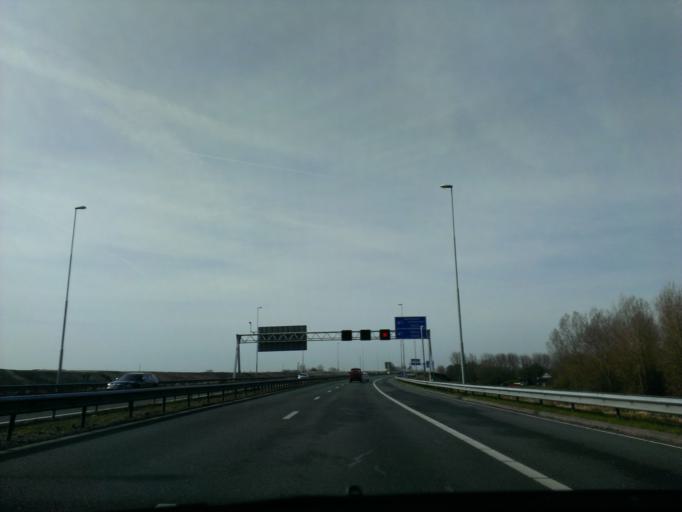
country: NL
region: North Holland
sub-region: Gemeente Amsterdam
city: Driemond
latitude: 52.3212
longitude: 5.0022
